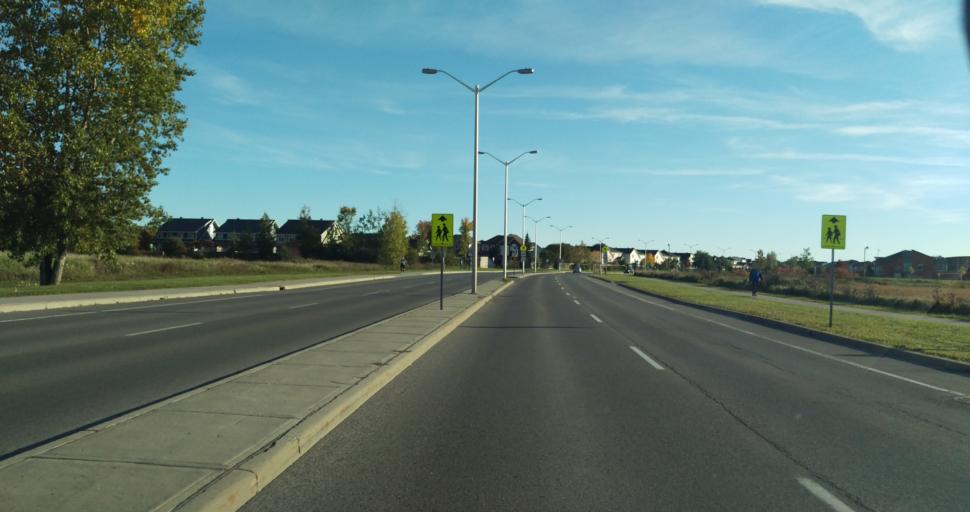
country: CA
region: Ontario
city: Clarence-Rockland
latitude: 45.4611
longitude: -75.4656
